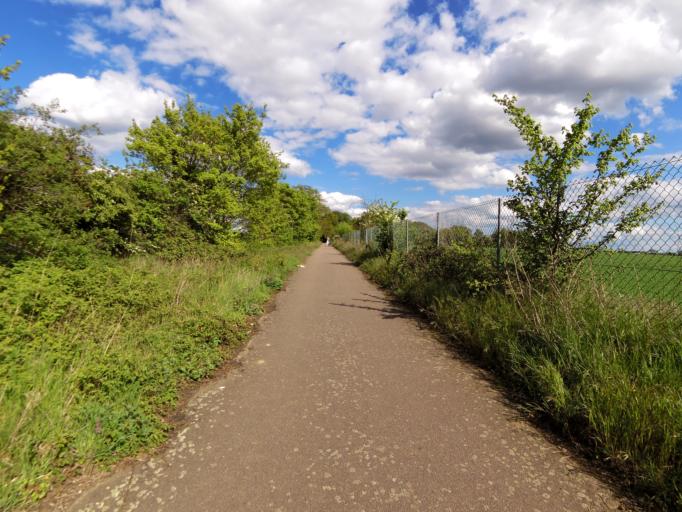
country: GB
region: England
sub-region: Suffolk
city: Great Barton
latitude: 52.2498
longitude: 0.7642
